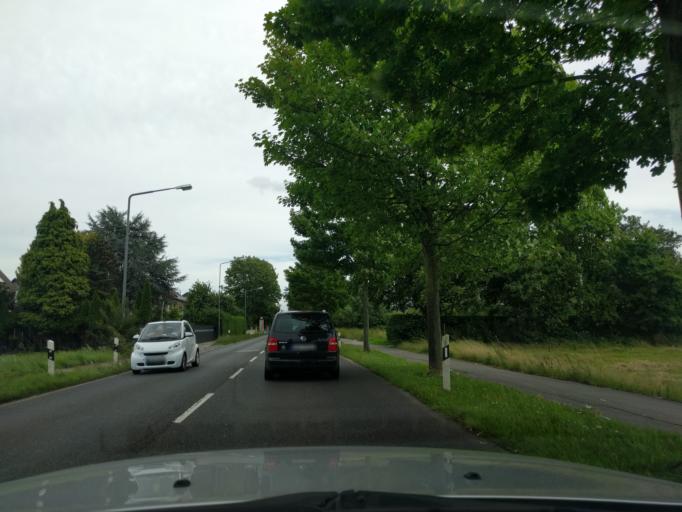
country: DE
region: North Rhine-Westphalia
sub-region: Regierungsbezirk Dusseldorf
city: Ratingen
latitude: 51.2999
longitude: 6.8137
